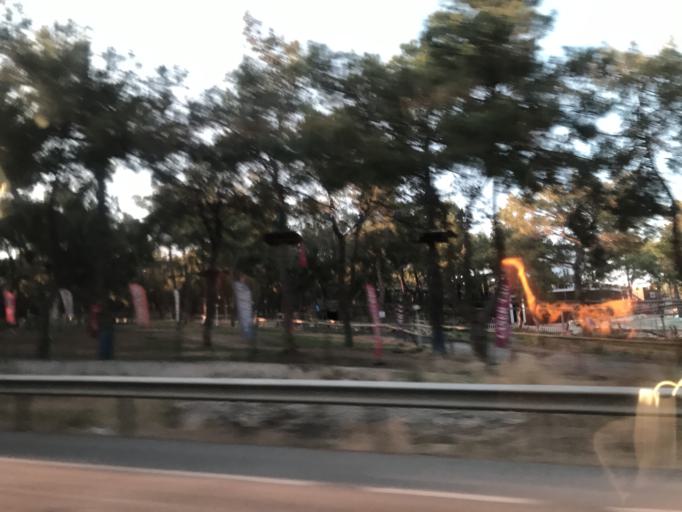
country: TR
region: Antalya
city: Antalya
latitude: 36.9479
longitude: 30.6411
